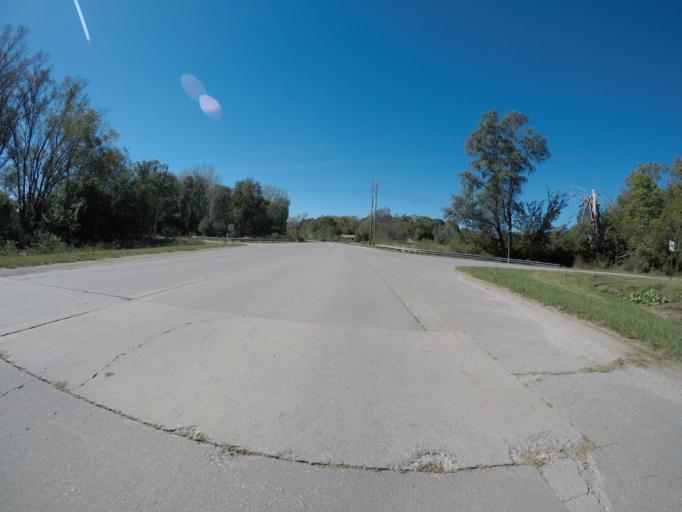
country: US
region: Kansas
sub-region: Wyandotte County
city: Bonner Springs
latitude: 39.0148
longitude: -94.9085
